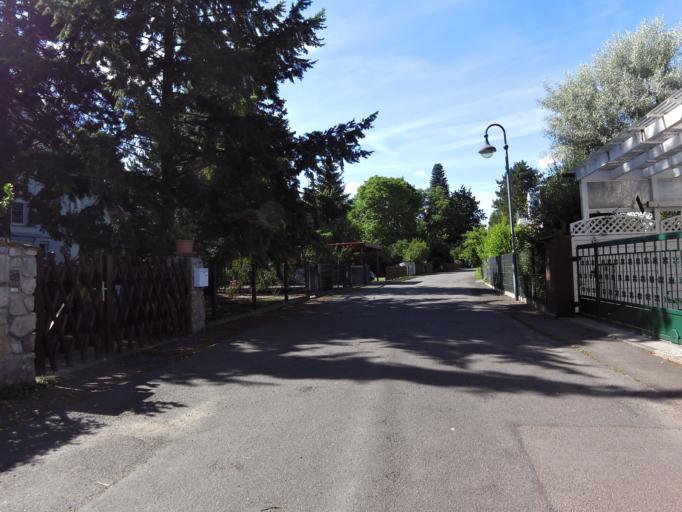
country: DE
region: Saxony
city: Leipzig
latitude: 51.3194
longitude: 12.4411
